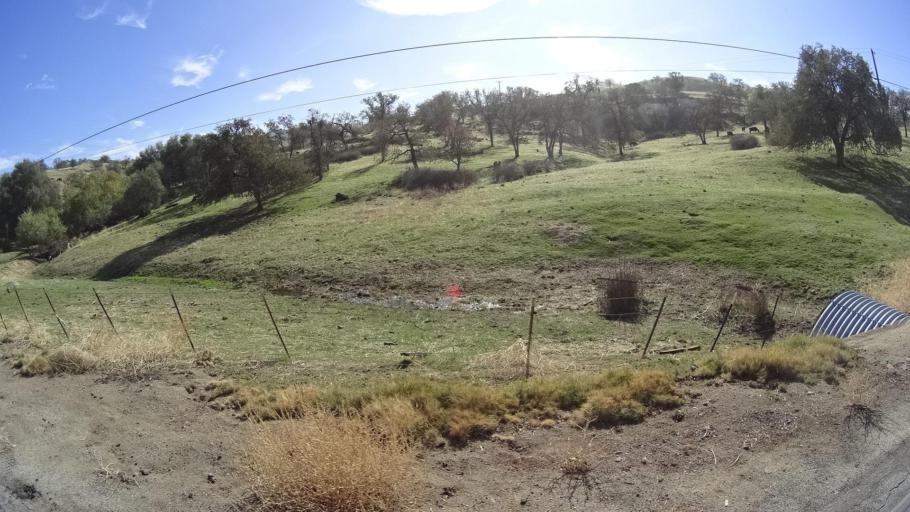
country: US
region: California
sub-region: Tulare County
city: Richgrove
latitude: 35.6997
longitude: -118.8402
